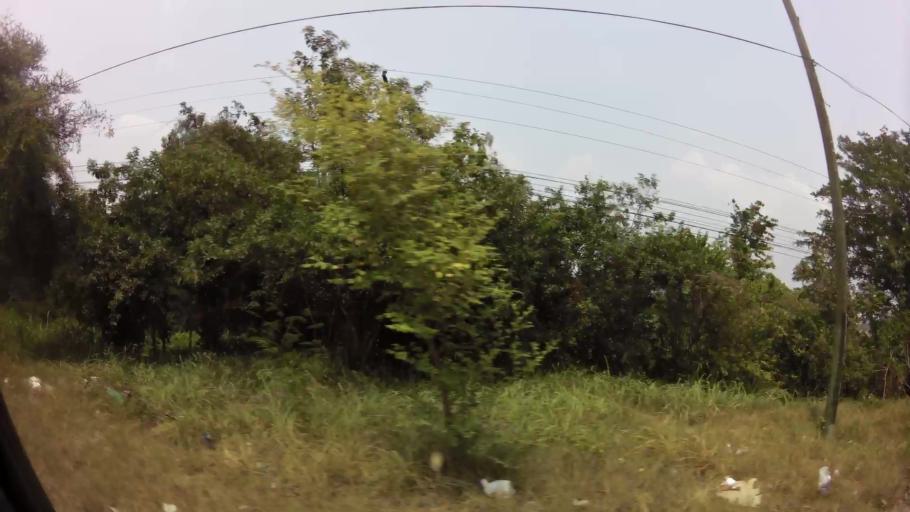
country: HN
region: Cortes
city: La Lima
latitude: 15.4249
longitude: -87.8985
